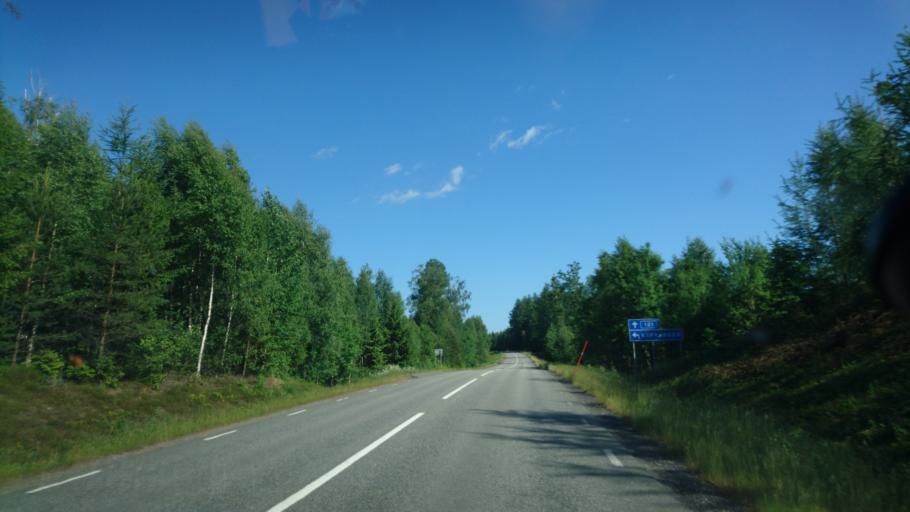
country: SE
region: Skane
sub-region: Osby Kommun
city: Lonsboda
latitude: 56.4337
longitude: 14.2582
